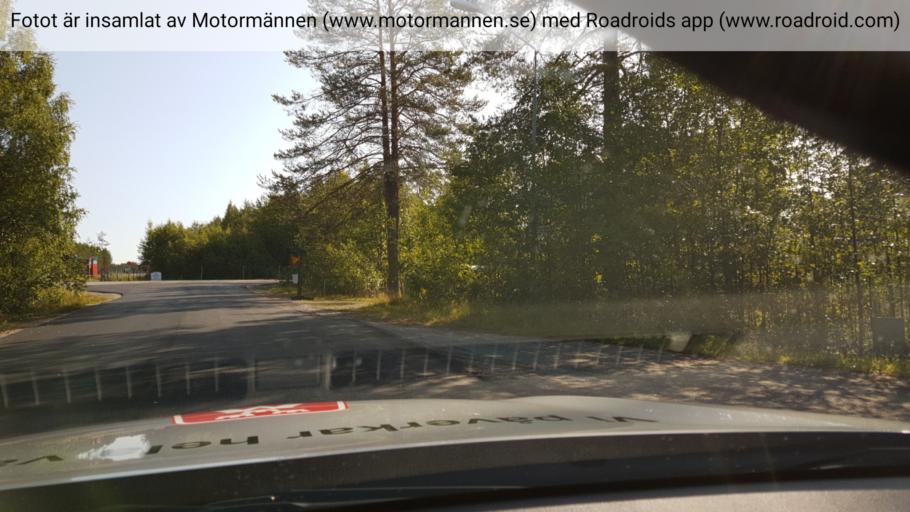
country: SE
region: Norrbotten
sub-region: Kalix Kommun
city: Toere
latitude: 65.9091
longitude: 22.6715
